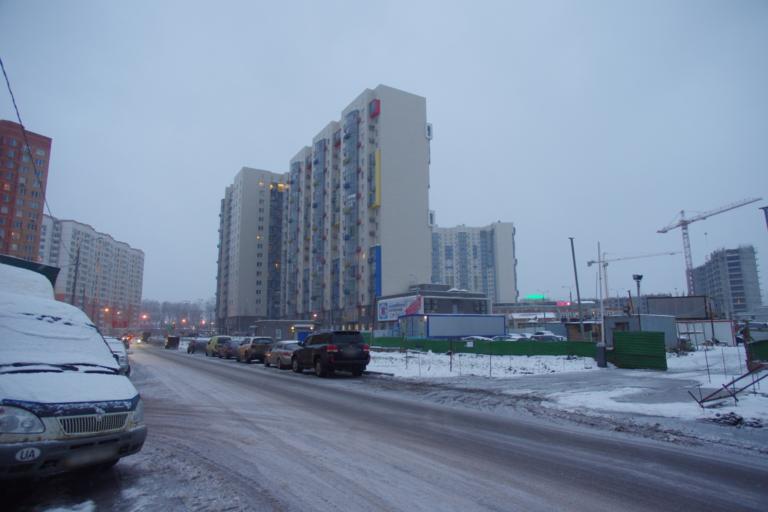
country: RU
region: Moskovskaya
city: Pavshino
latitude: 55.8249
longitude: 37.3727
